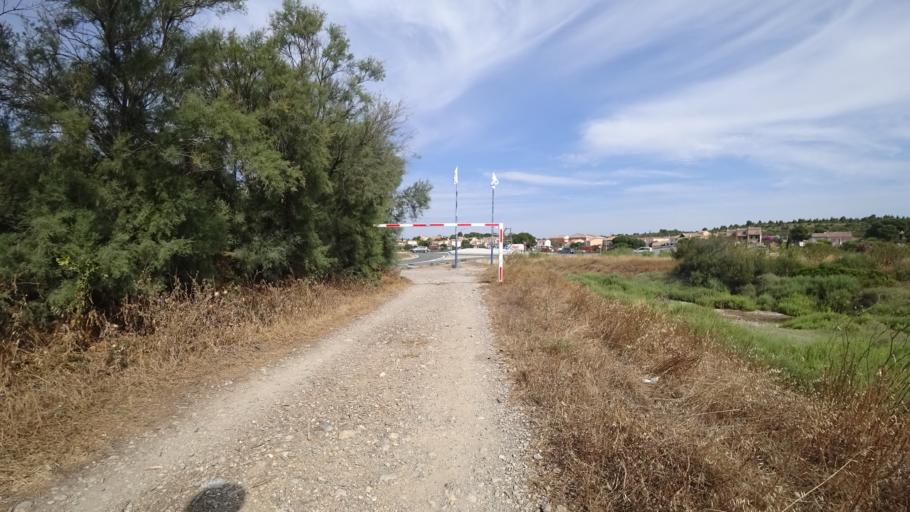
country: FR
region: Languedoc-Roussillon
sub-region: Departement de l'Aude
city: Leucate
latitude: 42.9046
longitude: 3.0381
